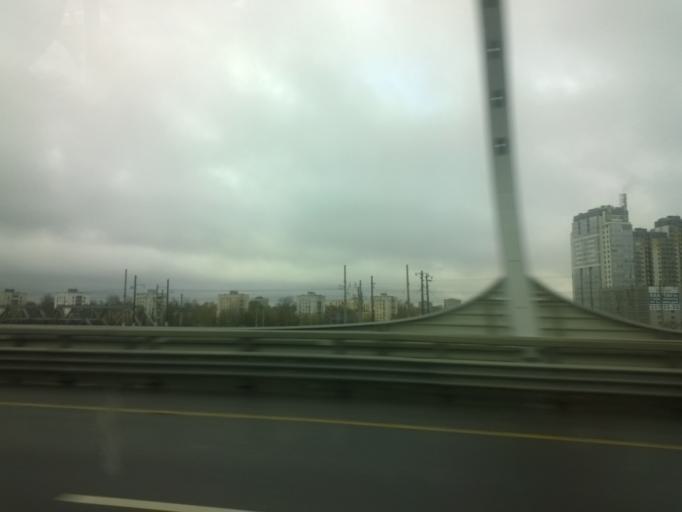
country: RU
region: St.-Petersburg
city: Dachnoye
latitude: 59.8469
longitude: 30.2871
